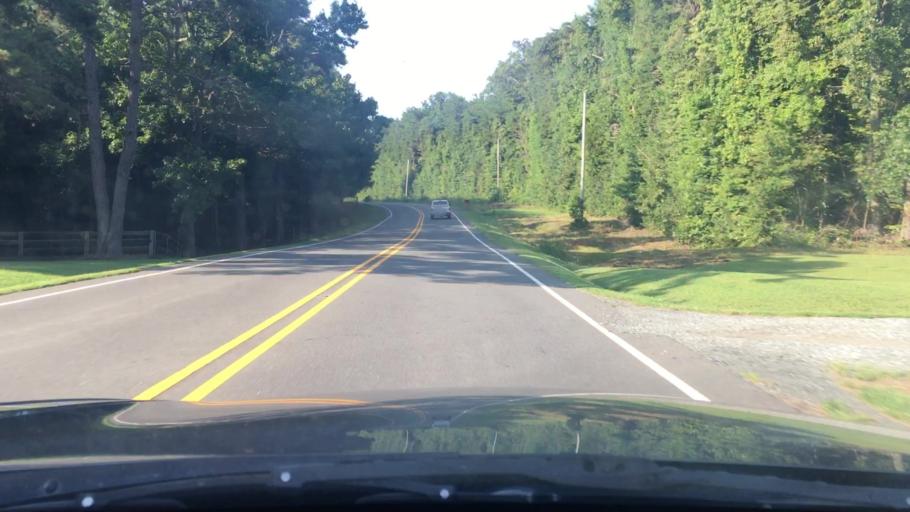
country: US
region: North Carolina
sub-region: Caswell County
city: Yanceyville
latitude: 36.2960
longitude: -79.3674
